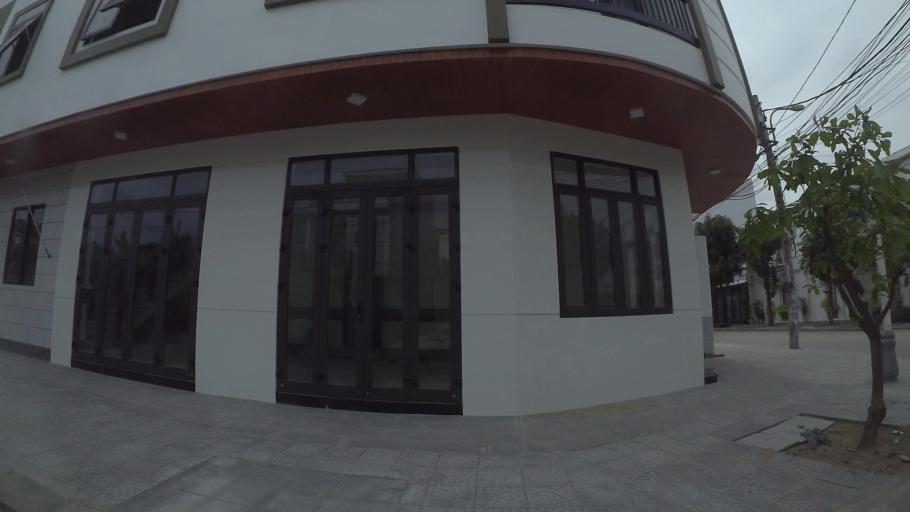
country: VN
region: Da Nang
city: Son Tra
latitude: 16.0639
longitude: 108.2407
